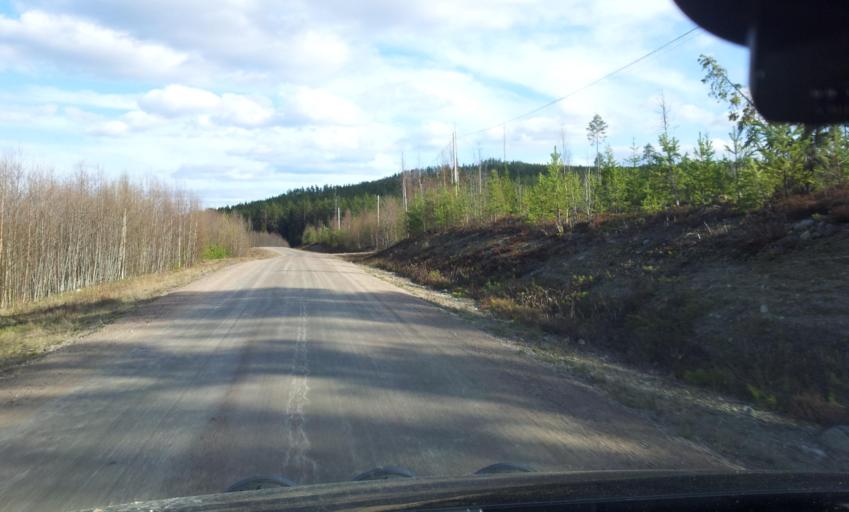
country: SE
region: Vaesternorrland
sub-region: Ange Kommun
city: Ange
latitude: 62.1715
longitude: 15.6440
